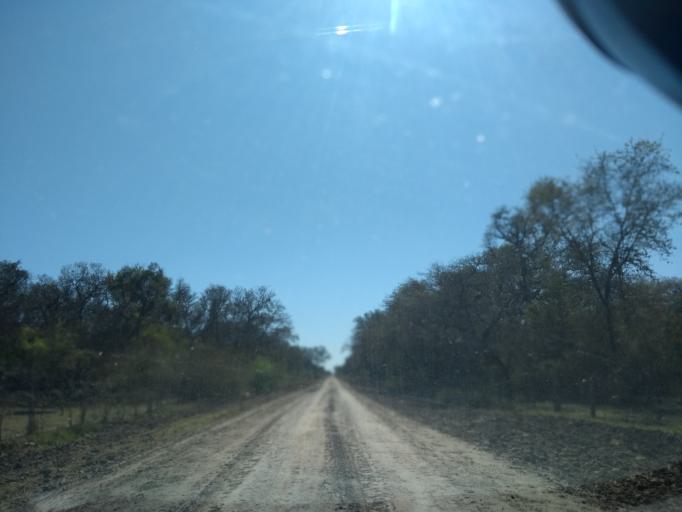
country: AR
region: Chaco
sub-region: Departamento de Quitilipi
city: Quitilipi
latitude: -26.7269
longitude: -60.2301
